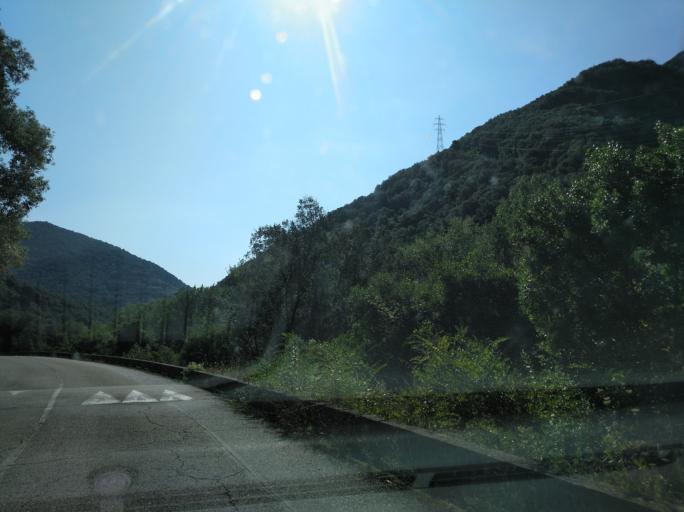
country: ES
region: Catalonia
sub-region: Provincia de Girona
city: la Cellera de Ter
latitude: 41.9858
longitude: 2.5727
